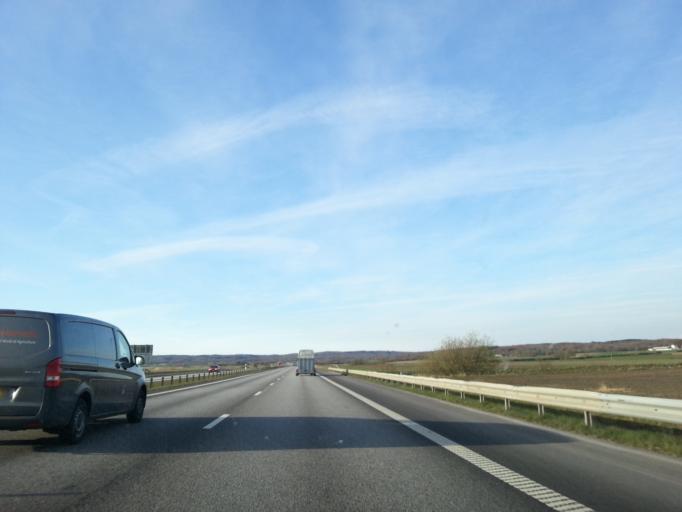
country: SE
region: Skane
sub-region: Angelholms Kommun
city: AEngelholm
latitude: 56.2829
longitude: 12.8990
